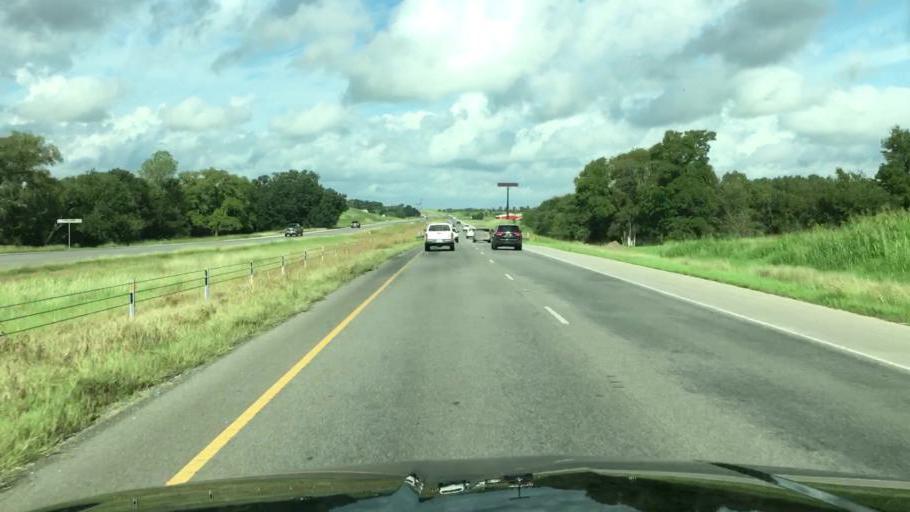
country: US
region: Texas
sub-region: Bastrop County
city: Wyldwood
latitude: 30.1628
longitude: -97.5059
